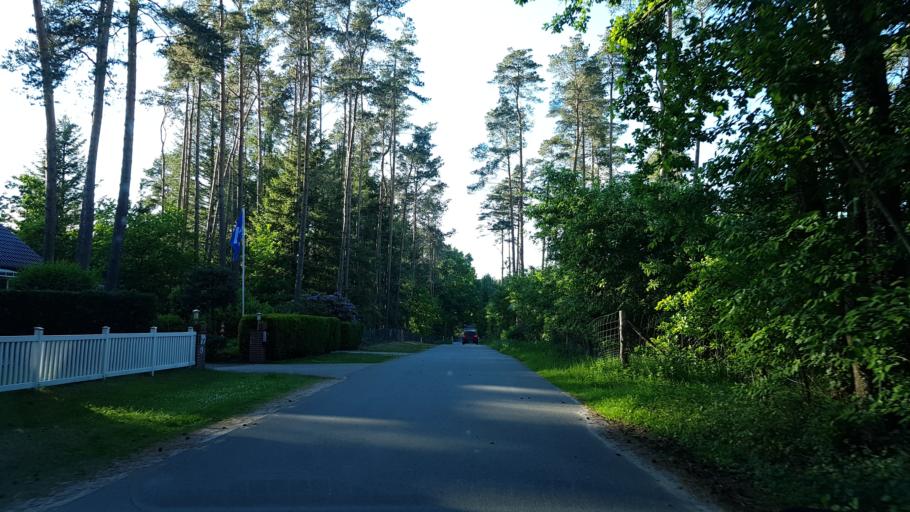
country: DE
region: Lower Saxony
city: Stelle
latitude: 53.3546
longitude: 10.1054
